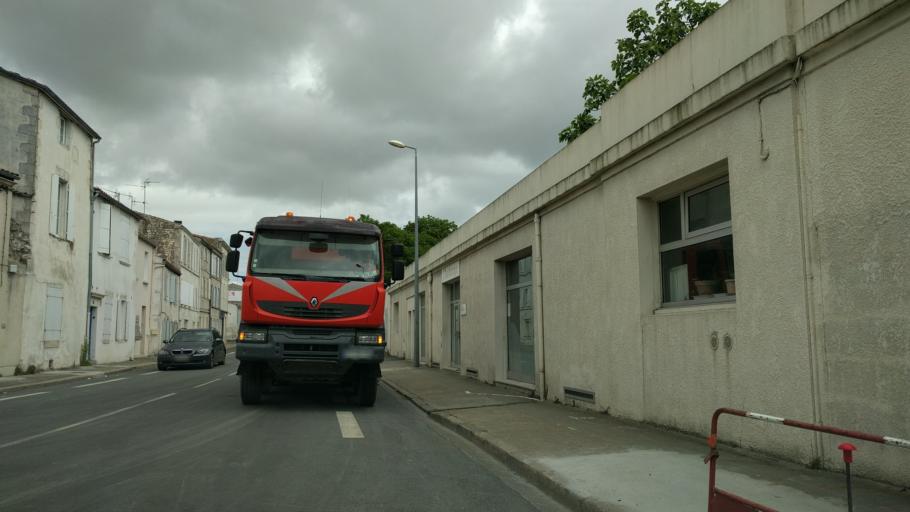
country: FR
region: Poitou-Charentes
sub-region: Departement de la Charente-Maritime
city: La Rochelle
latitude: 46.1631
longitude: -1.1457
